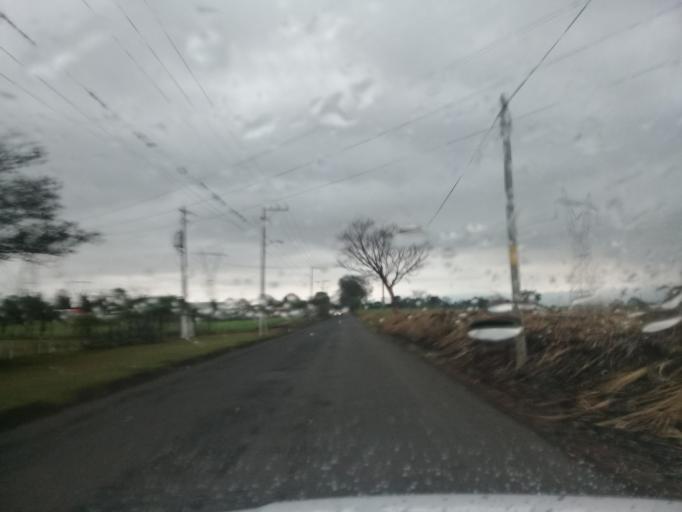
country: MX
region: Veracruz
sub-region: Cordoba
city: San Jose de Tapia
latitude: 18.8541
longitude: -96.9508
